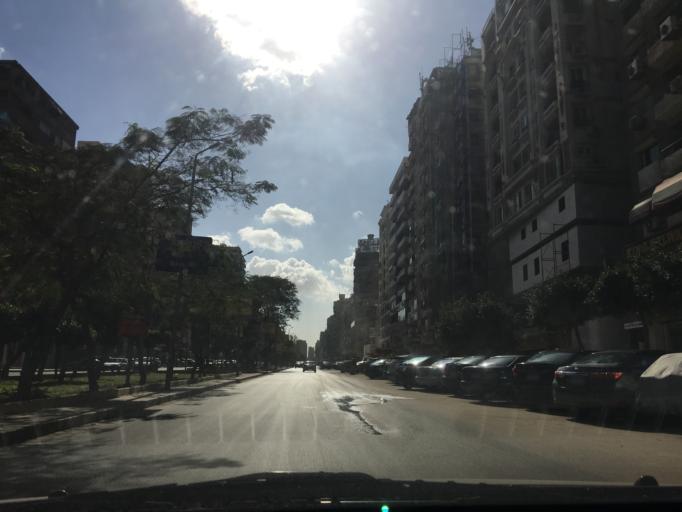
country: EG
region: Muhafazat al Qahirah
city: Cairo
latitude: 30.0599
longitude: 31.3453
